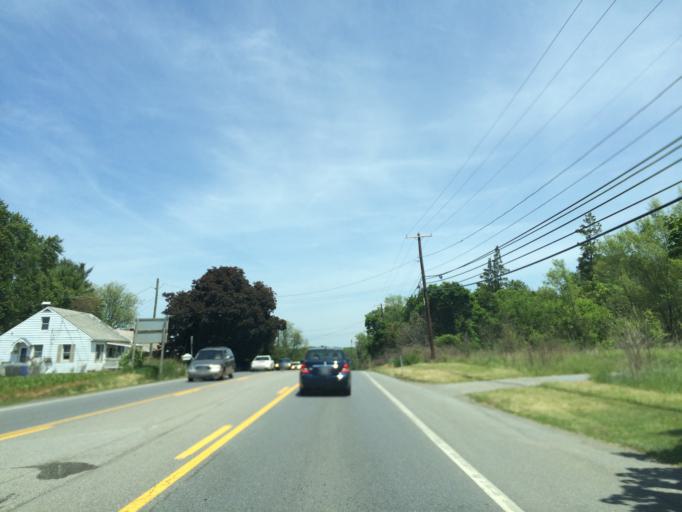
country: US
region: Maryland
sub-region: Washington County
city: Halfway
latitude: 39.5978
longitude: -77.7301
